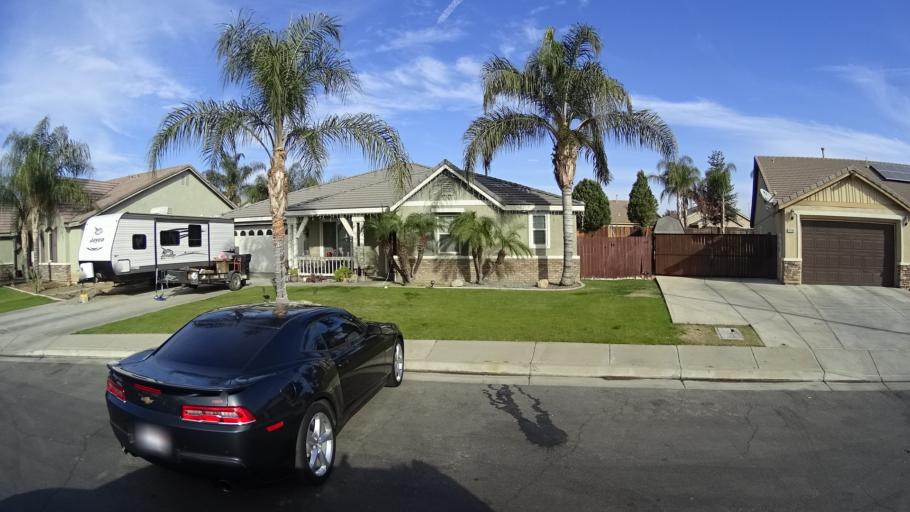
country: US
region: California
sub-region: Kern County
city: Rosedale
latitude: 35.4084
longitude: -119.1372
